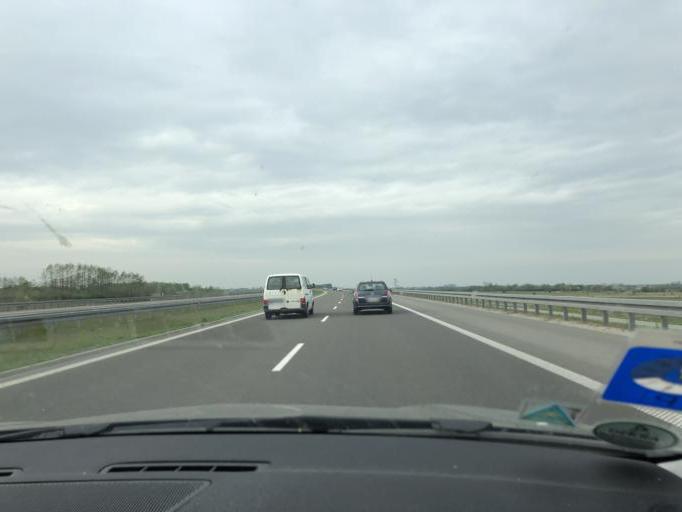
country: PL
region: Subcarpathian Voivodeship
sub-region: Powiat rzeszowski
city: Wolka Podlesna
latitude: 50.0959
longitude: 22.1256
